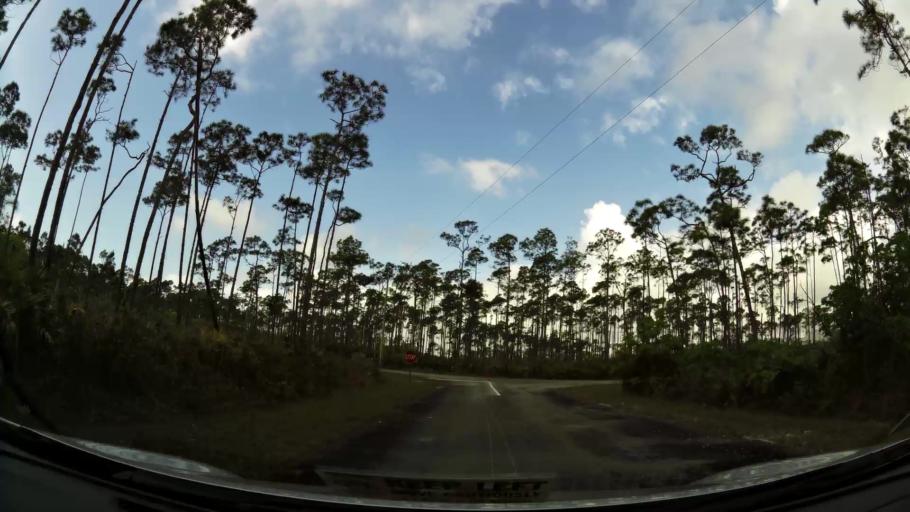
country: BS
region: Freeport
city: Lucaya
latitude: 26.5862
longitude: -78.5528
